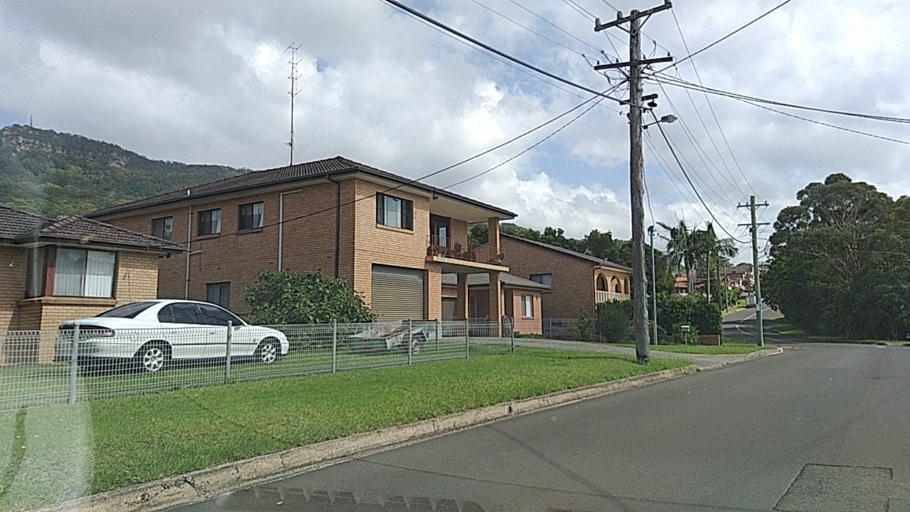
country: AU
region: New South Wales
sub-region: Wollongong
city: Corrimal
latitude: -34.3752
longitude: 150.8894
